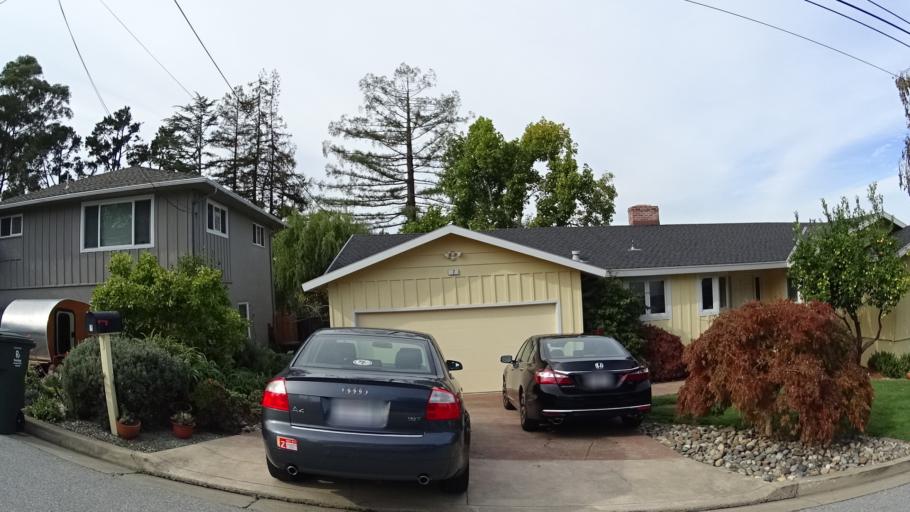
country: US
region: California
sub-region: San Mateo County
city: Hillsborough
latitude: 37.5759
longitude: -122.3849
